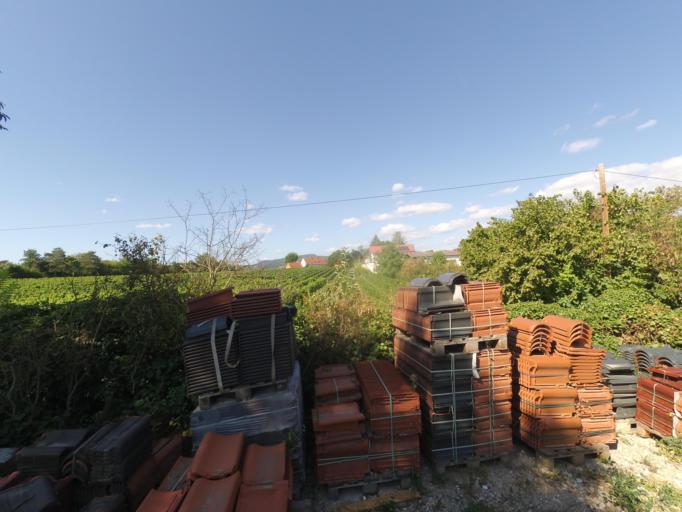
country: DE
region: Rheinland-Pfalz
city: Freinsheim
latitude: 49.5005
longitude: 8.2052
